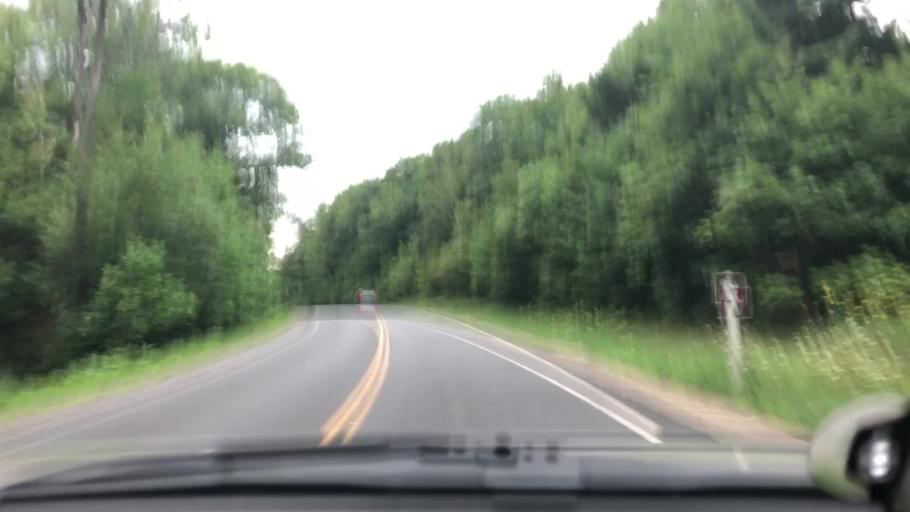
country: US
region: New York
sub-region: Saratoga County
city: Corinth
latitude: 43.2032
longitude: -73.7677
